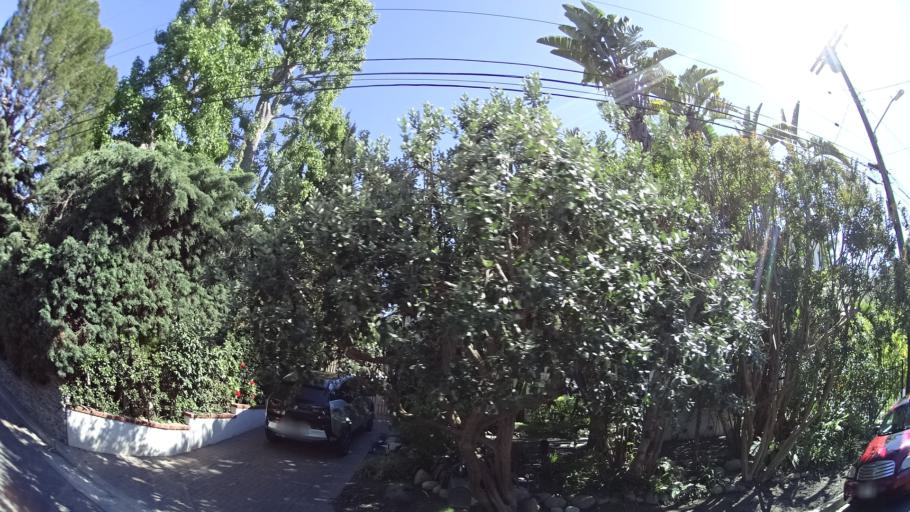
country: US
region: California
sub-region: Los Angeles County
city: Sherman Oaks
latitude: 34.1467
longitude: -118.4555
